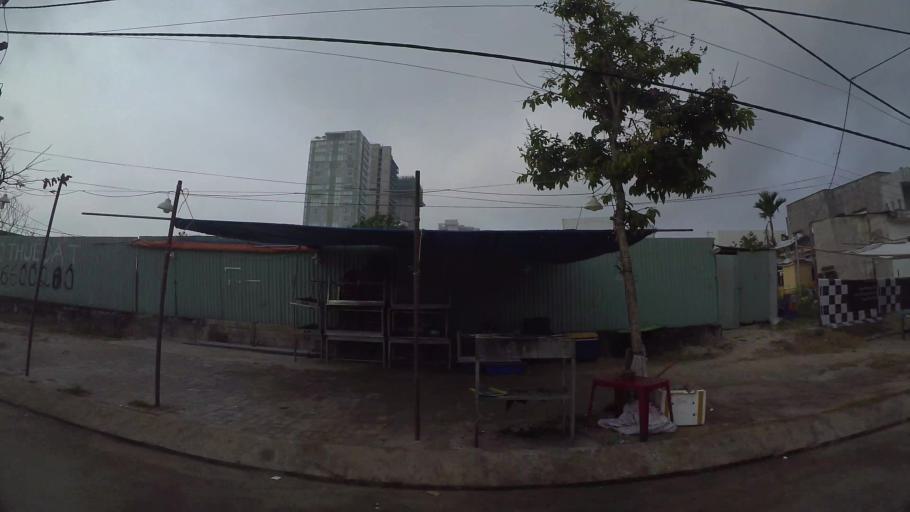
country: VN
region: Da Nang
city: Son Tra
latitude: 16.0827
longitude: 108.2471
